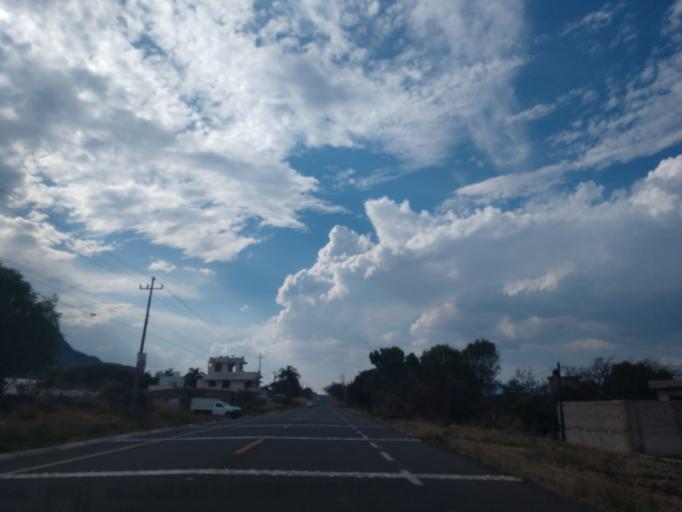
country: MX
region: Jalisco
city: Chapala
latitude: 20.1714
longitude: -103.2165
